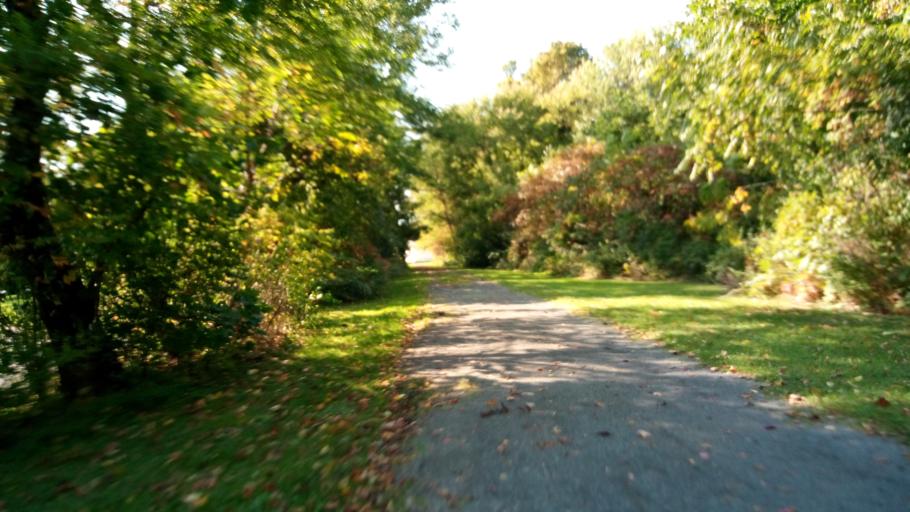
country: US
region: New York
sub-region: Wayne County
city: Clyde
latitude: 43.0817
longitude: -76.8756
